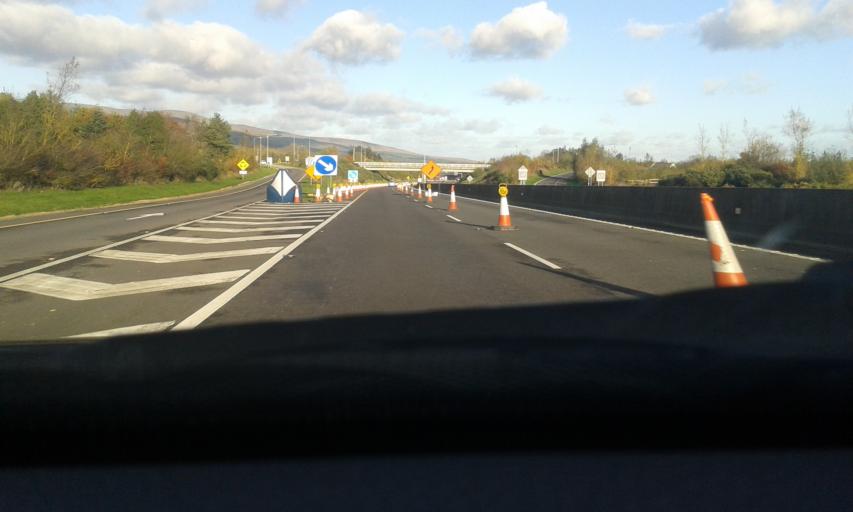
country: IE
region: Munster
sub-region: County Cork
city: Mitchelstown
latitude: 52.2826
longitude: -8.2217
